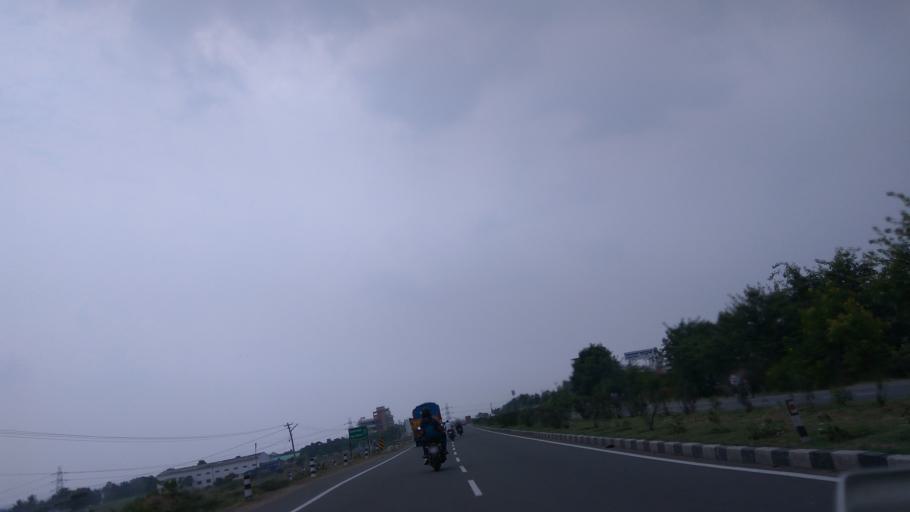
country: IN
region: Tamil Nadu
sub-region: Dharmapuri
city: Dharmapuri
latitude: 12.1834
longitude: 78.1759
